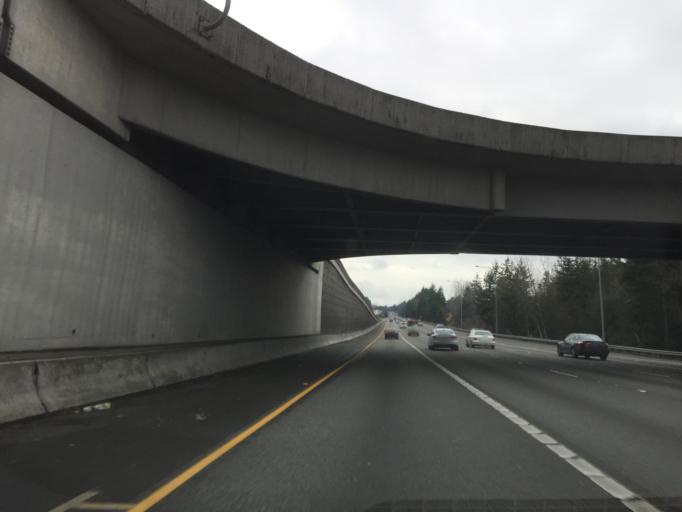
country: US
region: Washington
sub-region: Snohomish County
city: Alderwood Manor
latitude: 47.8134
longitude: -122.2936
